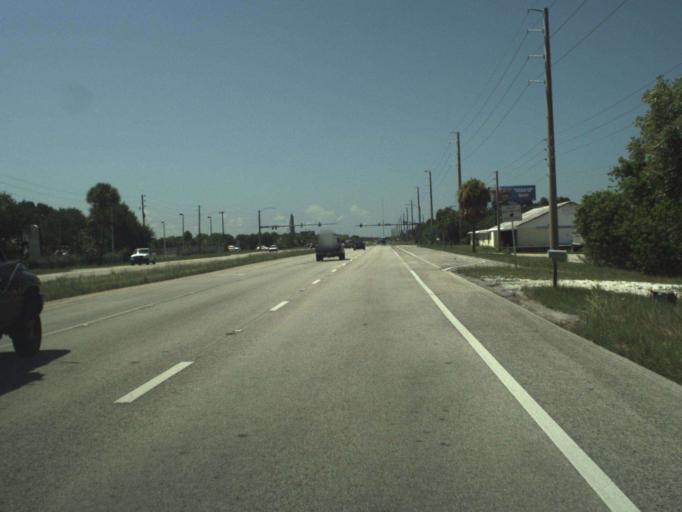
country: US
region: Florida
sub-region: Saint Lucie County
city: Lakewood Park
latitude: 27.5184
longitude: -80.3544
